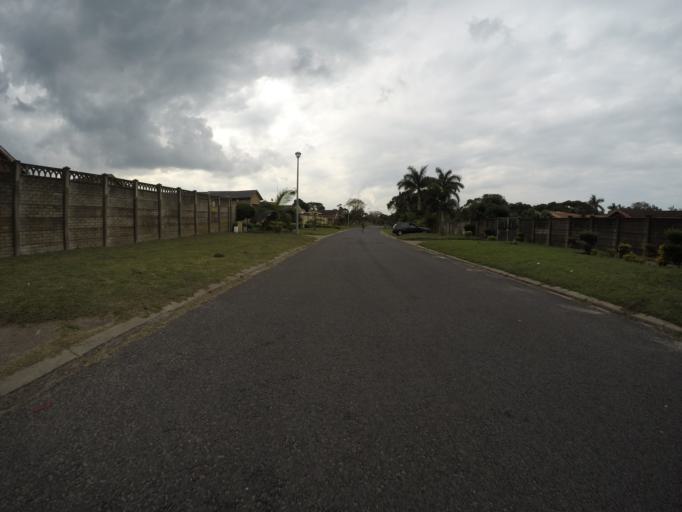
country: ZA
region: KwaZulu-Natal
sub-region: uThungulu District Municipality
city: Richards Bay
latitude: -28.7378
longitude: 32.0520
